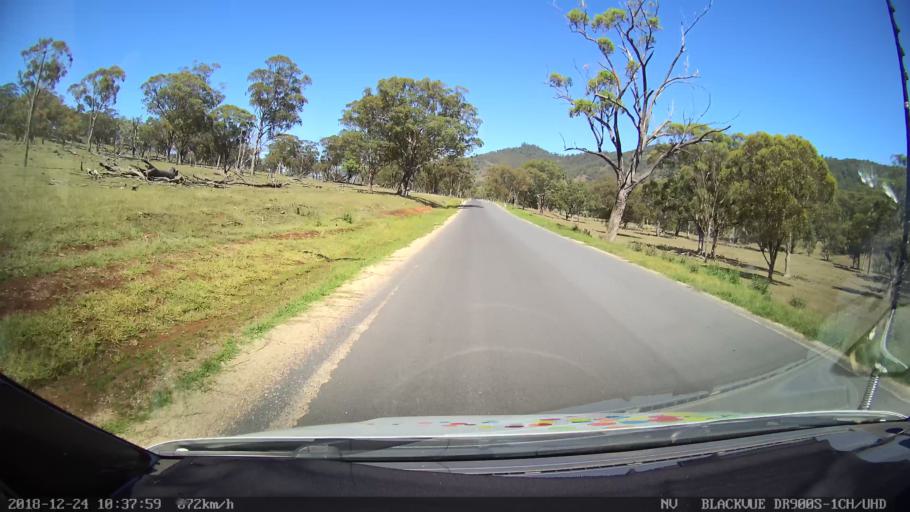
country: AU
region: New South Wales
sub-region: Upper Hunter Shire
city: Merriwa
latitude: -31.8475
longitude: 150.4870
